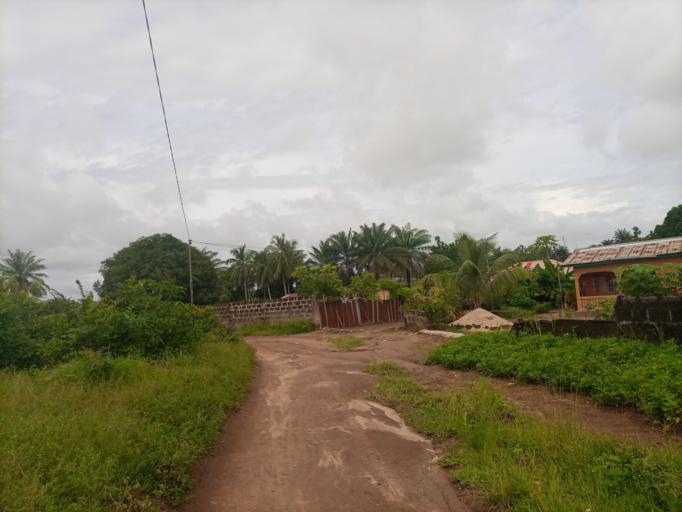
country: SL
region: Northern Province
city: Masoyila
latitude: 8.5952
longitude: -13.1776
